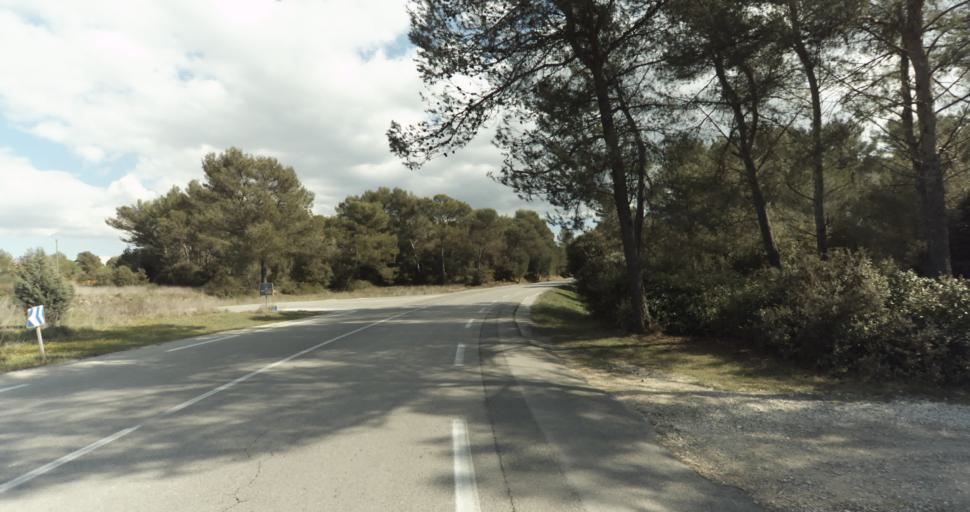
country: FR
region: Provence-Alpes-Cote d'Azur
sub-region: Departement des Bouches-du-Rhone
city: Greasque
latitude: 43.4459
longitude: 5.5231
